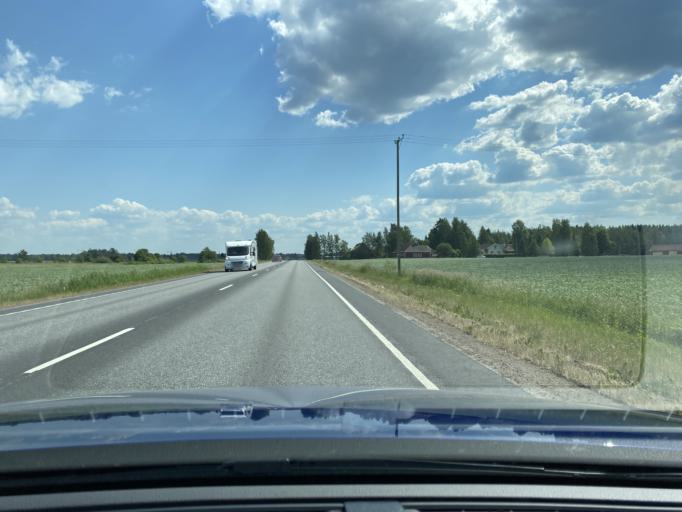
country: FI
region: Satakunta
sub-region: Rauma
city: Eura
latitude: 61.1519
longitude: 22.0975
